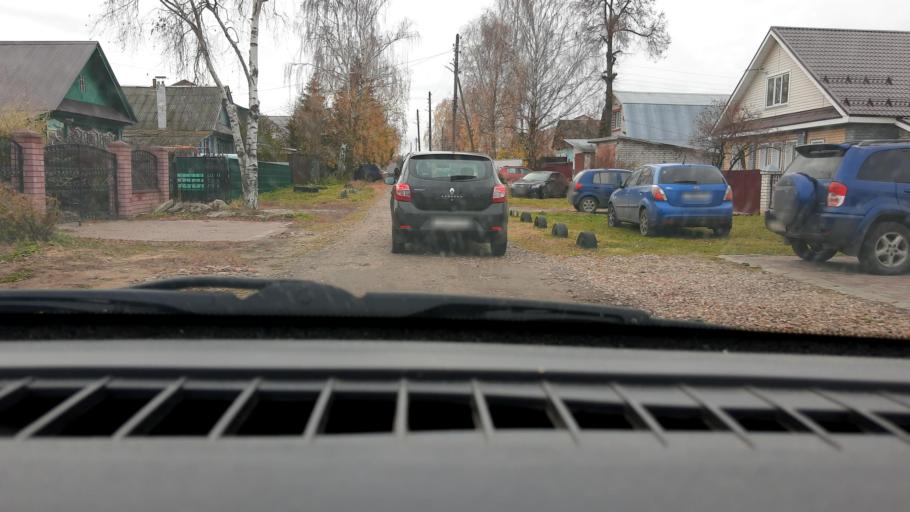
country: RU
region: Nizjnij Novgorod
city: Lukino
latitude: 56.4041
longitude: 43.7199
